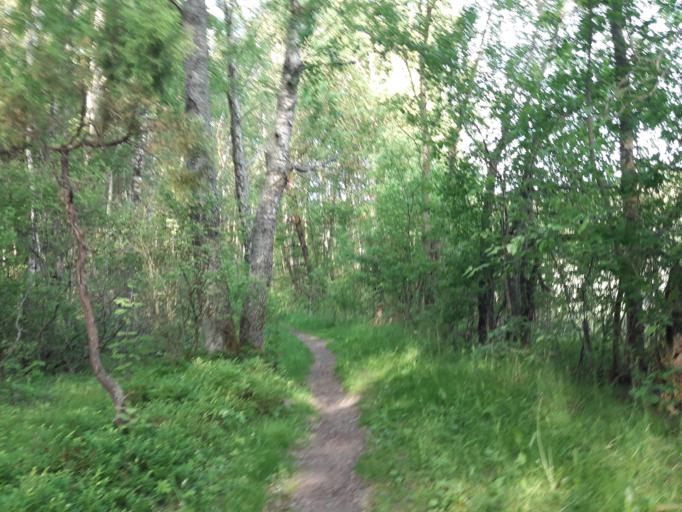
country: BY
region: Minsk
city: Pyatryshki
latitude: 54.1270
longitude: 27.1286
